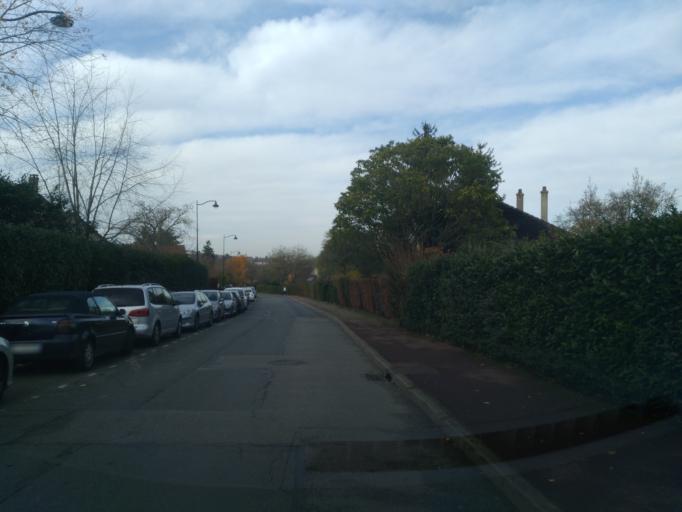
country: FR
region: Ile-de-France
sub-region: Departement des Yvelines
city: Fourqueux
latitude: 48.8891
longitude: 2.0679
